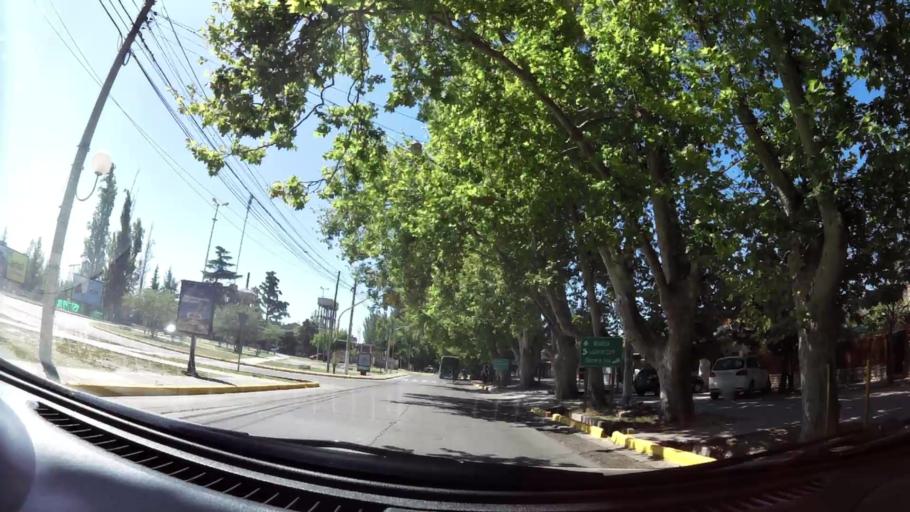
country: AR
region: Mendoza
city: Lujan de Cuyo
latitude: -32.9820
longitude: -68.8601
